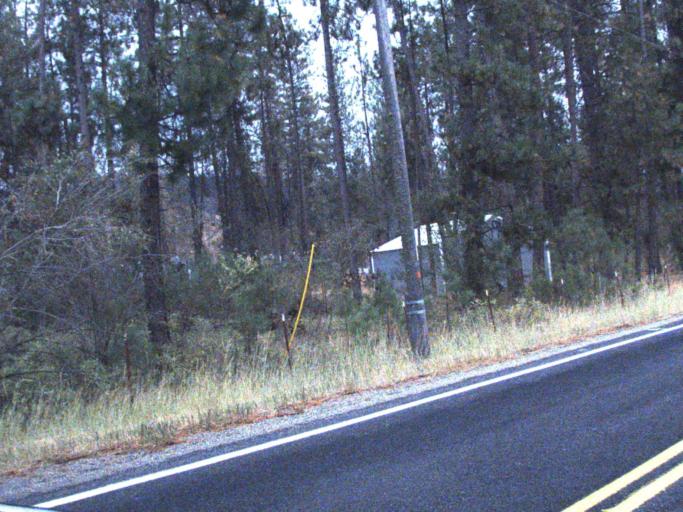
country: US
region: Washington
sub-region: Spokane County
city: Deer Park
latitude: 47.9619
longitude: -117.7465
